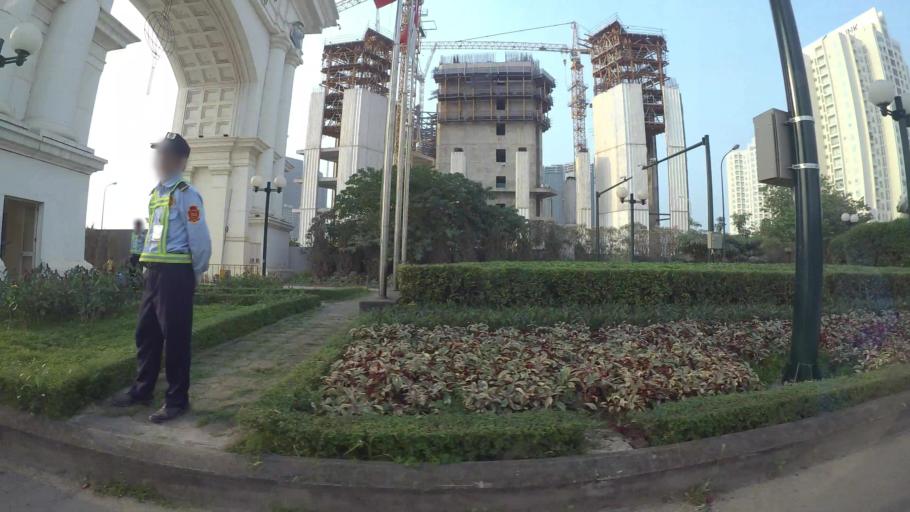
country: VN
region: Ha Noi
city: Tay Ho
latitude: 21.0810
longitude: 105.7902
